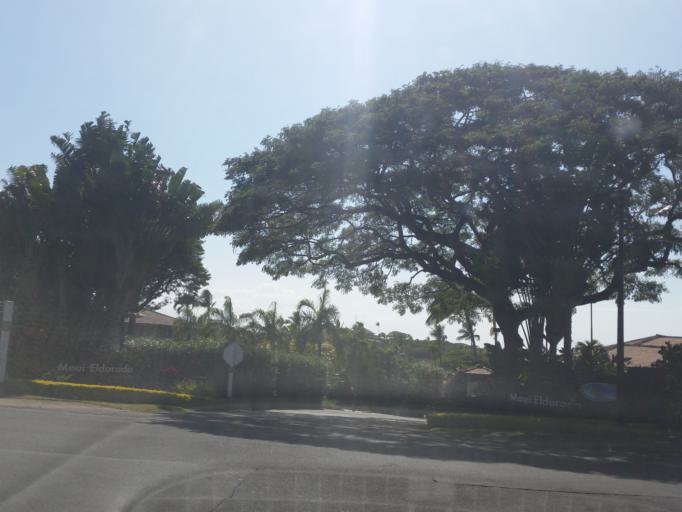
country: US
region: Hawaii
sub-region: Maui County
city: Ka'anapali
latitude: 20.9278
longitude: -156.6904
